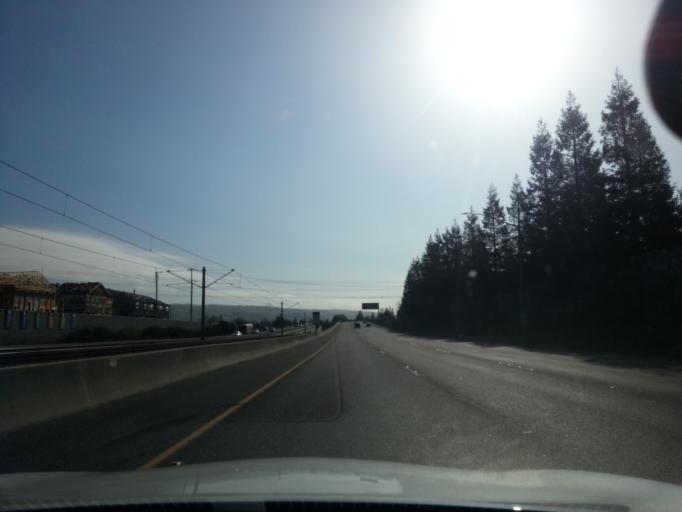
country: US
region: California
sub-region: Santa Clara County
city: Seven Trees
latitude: 37.2409
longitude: -121.7967
